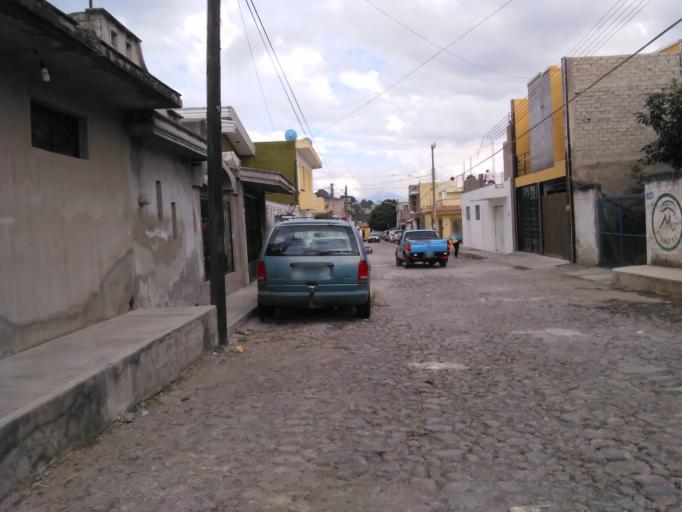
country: MX
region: Nayarit
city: Tepic
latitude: 21.5263
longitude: -104.9211
